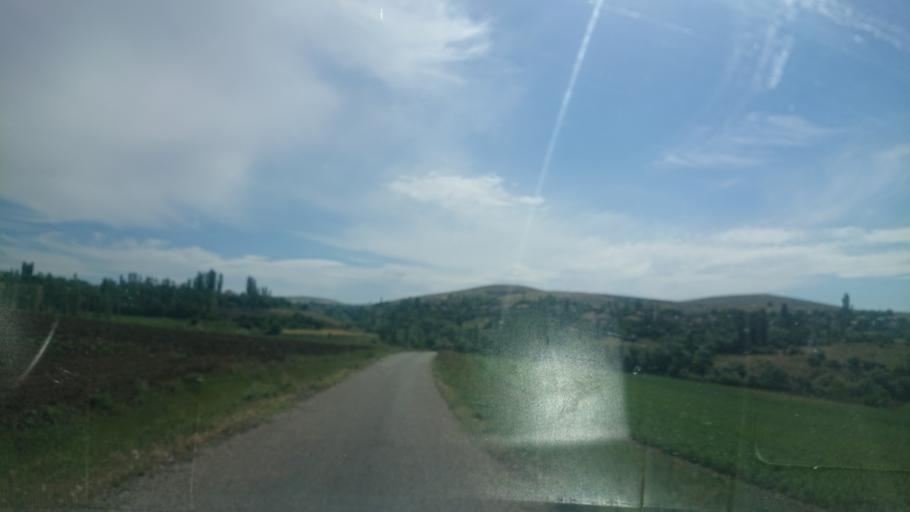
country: TR
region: Aksaray
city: Ortakoy
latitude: 38.8111
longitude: 33.9918
